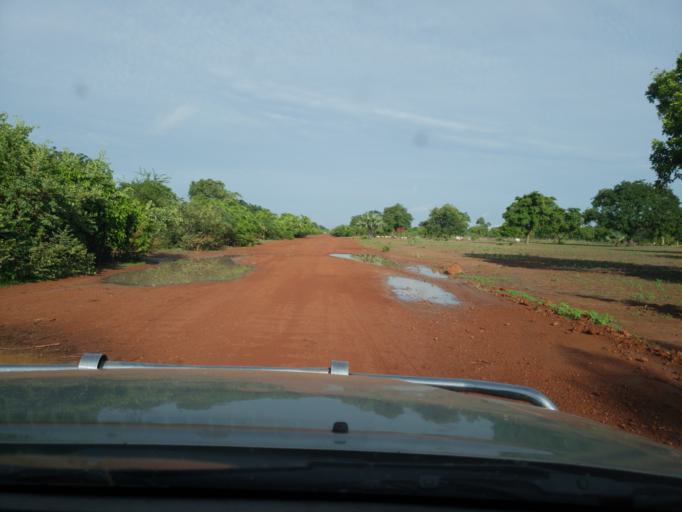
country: ML
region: Sikasso
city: Koutiala
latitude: 12.4181
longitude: -5.7079
